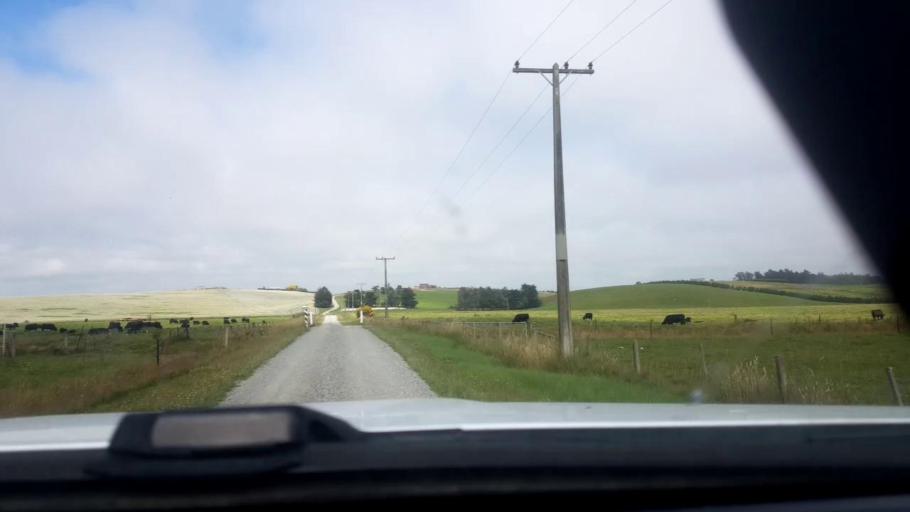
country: NZ
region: Canterbury
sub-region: Timaru District
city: Timaru
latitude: -44.3286
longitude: 171.2043
